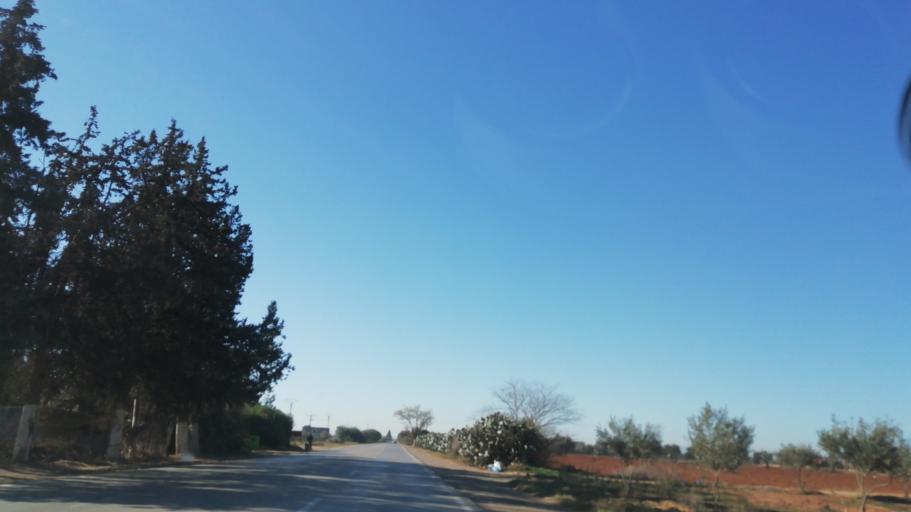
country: DZ
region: Tlemcen
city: Nedroma
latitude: 34.8295
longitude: -1.7905
